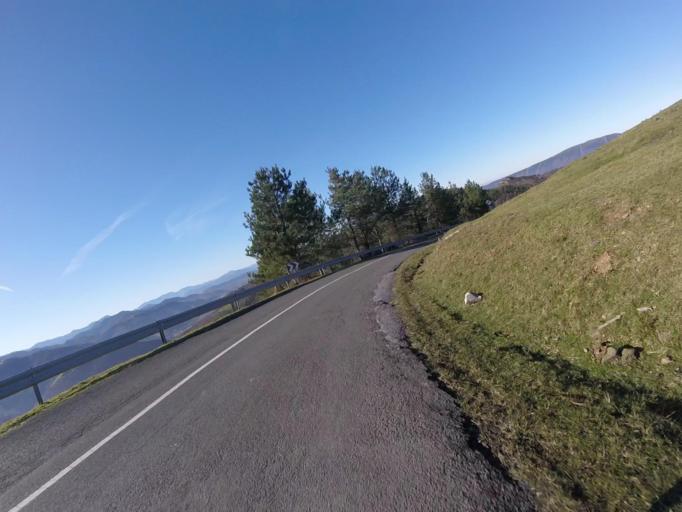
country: ES
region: Basque Country
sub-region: Provincia de Guipuzcoa
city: Irun
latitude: 43.2921
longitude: -1.8082
